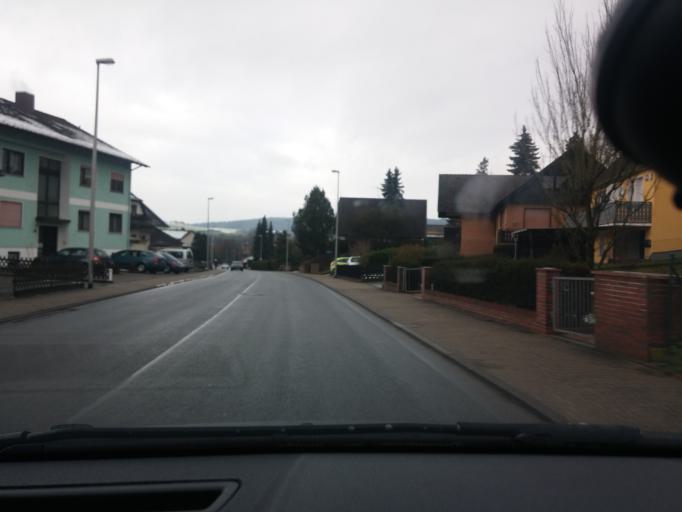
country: DE
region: Hesse
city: Michelstadt
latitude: 49.6855
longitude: 9.0123
